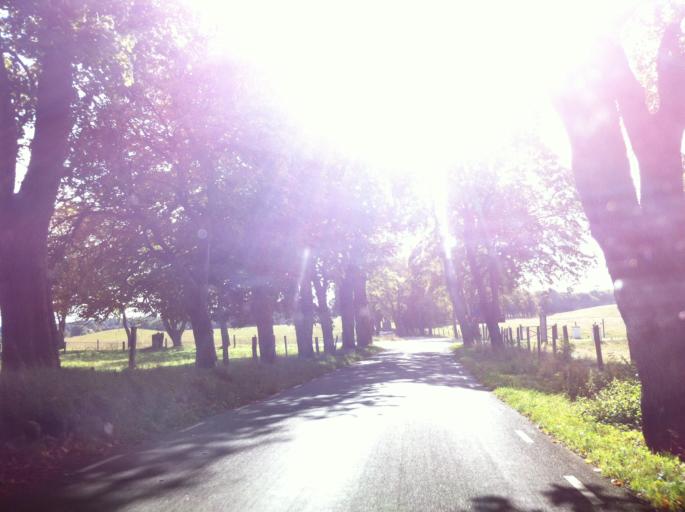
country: SE
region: Skane
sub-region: Kristianstads Kommun
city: Degeberga
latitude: 55.7145
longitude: 13.9702
